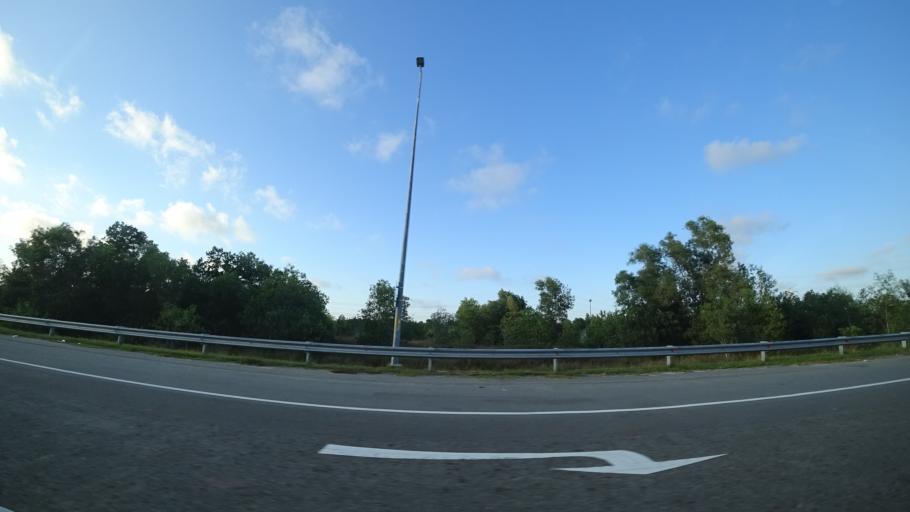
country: BN
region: Tutong
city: Tutong
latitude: 4.7440
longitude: 114.6008
